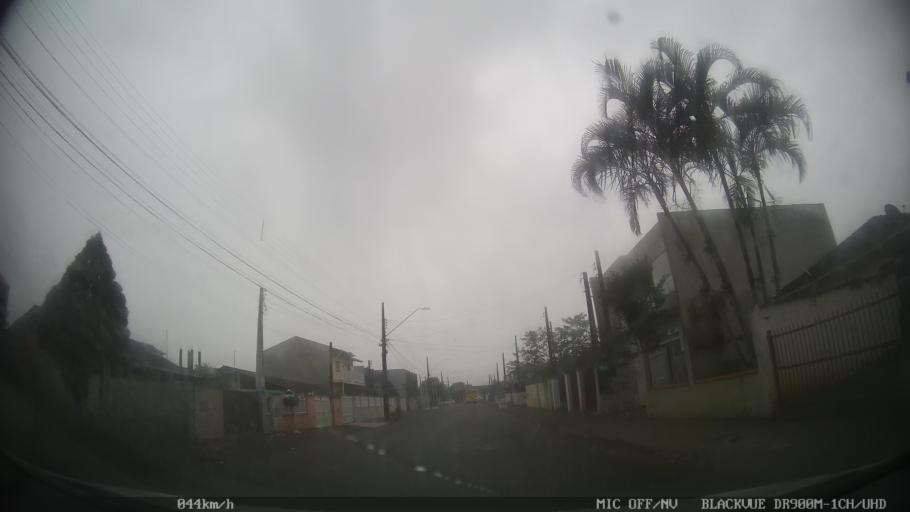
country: BR
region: Santa Catarina
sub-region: Joinville
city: Joinville
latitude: -26.2088
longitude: -48.8317
